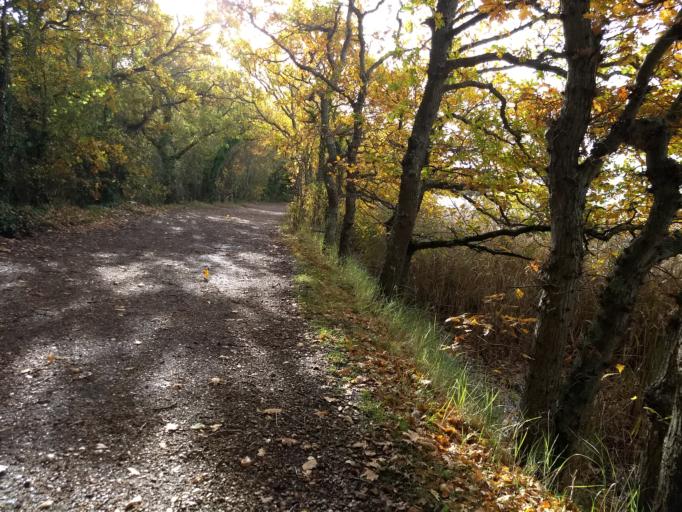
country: GB
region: England
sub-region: Isle of Wight
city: Freshwater
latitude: 50.6866
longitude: -1.5018
